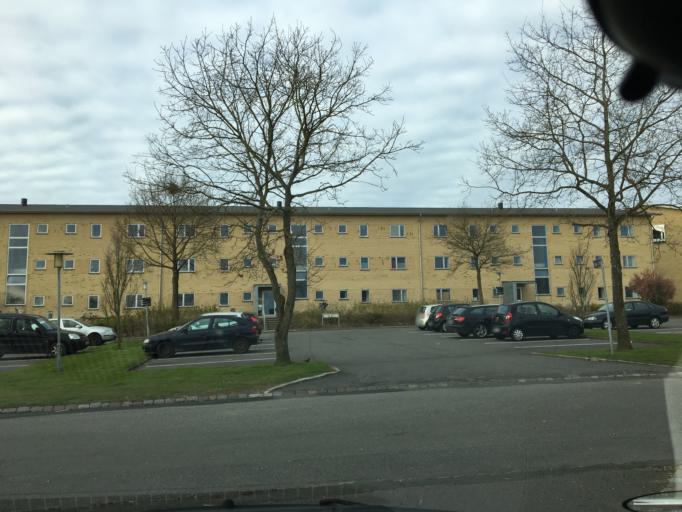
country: DK
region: South Denmark
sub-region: Vejle Kommune
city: Vejle
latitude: 55.6782
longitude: 9.5351
